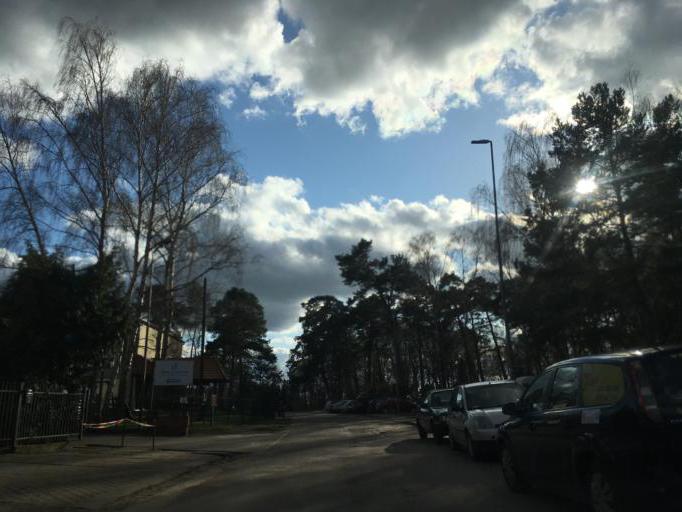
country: PL
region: Pomeranian Voivodeship
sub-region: Powiat gdanski
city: Cedry Wielkie
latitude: 54.3448
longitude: 18.8351
